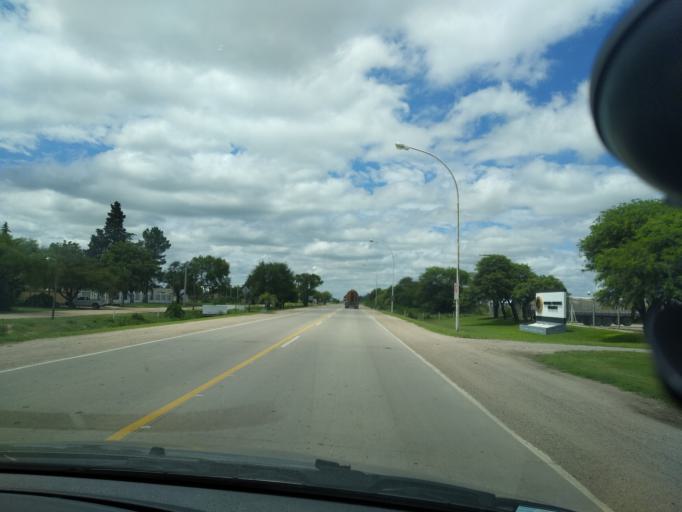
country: AR
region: Cordoba
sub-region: Departamento de Rio Segundo
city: Rio Segundo
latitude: -31.6437
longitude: -63.8997
